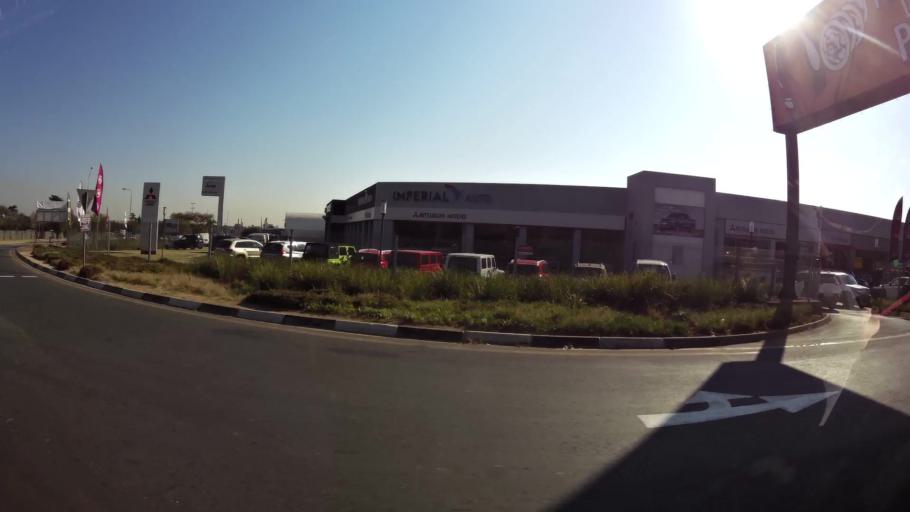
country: ZA
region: Gauteng
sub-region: City of Johannesburg Metropolitan Municipality
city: Modderfontein
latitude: -26.1600
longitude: 28.1671
